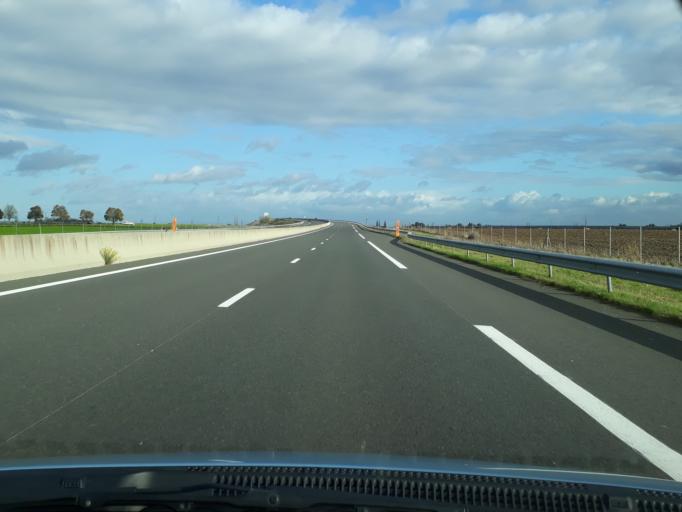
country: FR
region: Centre
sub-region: Departement du Loiret
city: Chevilly
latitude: 48.0447
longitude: 1.8664
